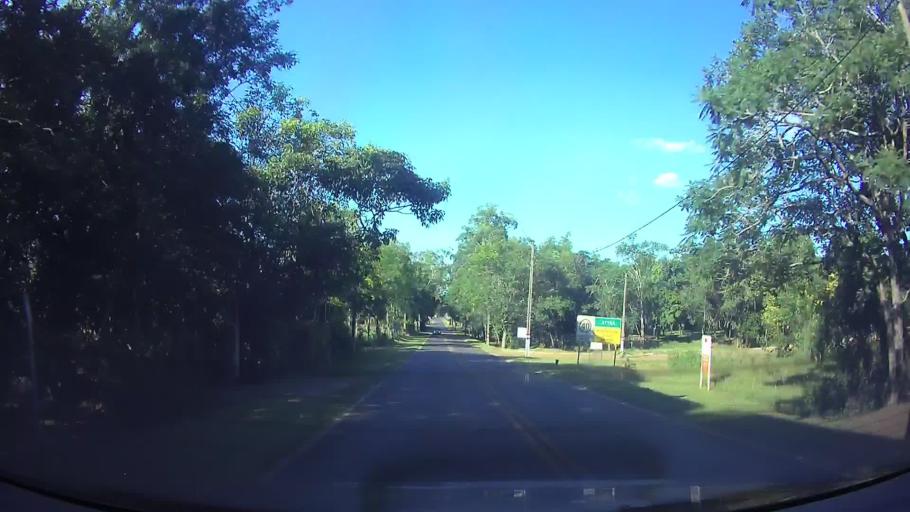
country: PY
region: Cordillera
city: Atyra
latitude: -25.2881
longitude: -57.1790
